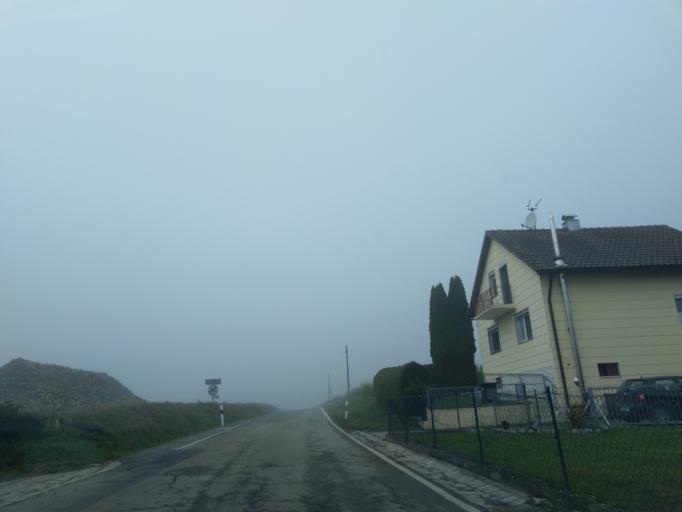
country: DE
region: Bavaria
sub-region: Lower Bavaria
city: Iggensbach
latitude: 48.7609
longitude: 13.1279
